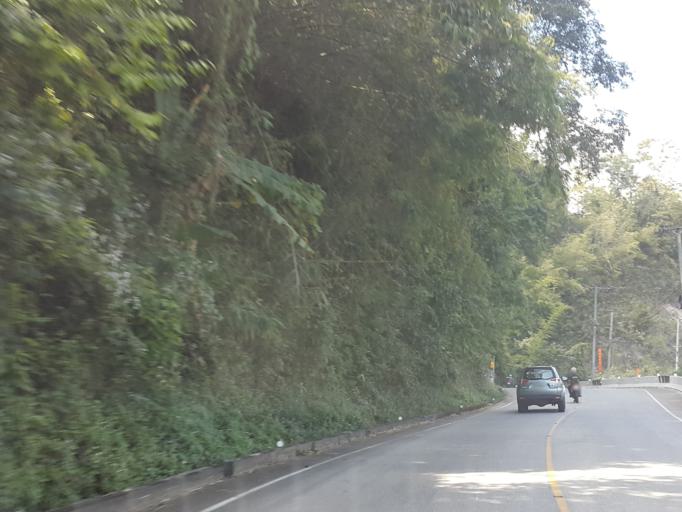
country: TH
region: Chiang Mai
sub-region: Amphoe Chiang Dao
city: Chiang Dao
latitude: 19.2995
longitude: 98.9575
